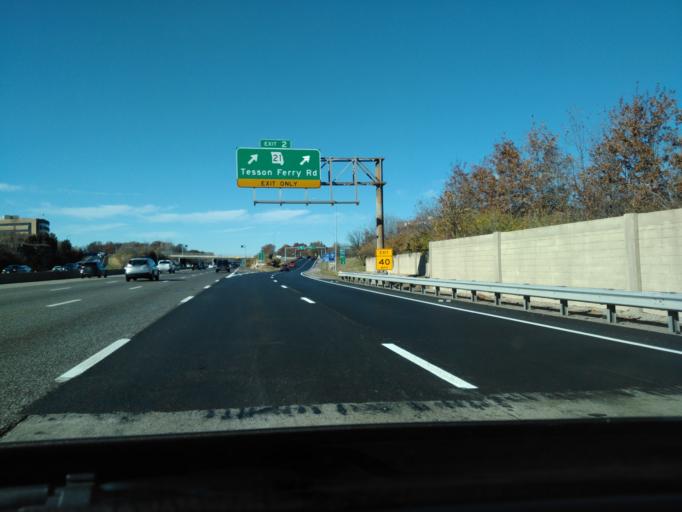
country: US
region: Missouri
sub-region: Saint Louis County
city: Concord
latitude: 38.5120
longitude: -90.3668
